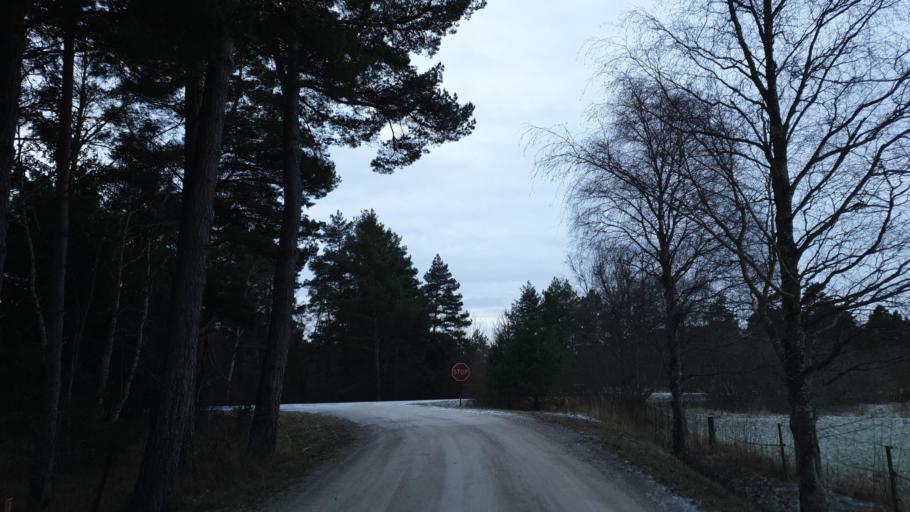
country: SE
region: Gotland
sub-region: Gotland
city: Slite
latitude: 57.4293
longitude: 18.8111
